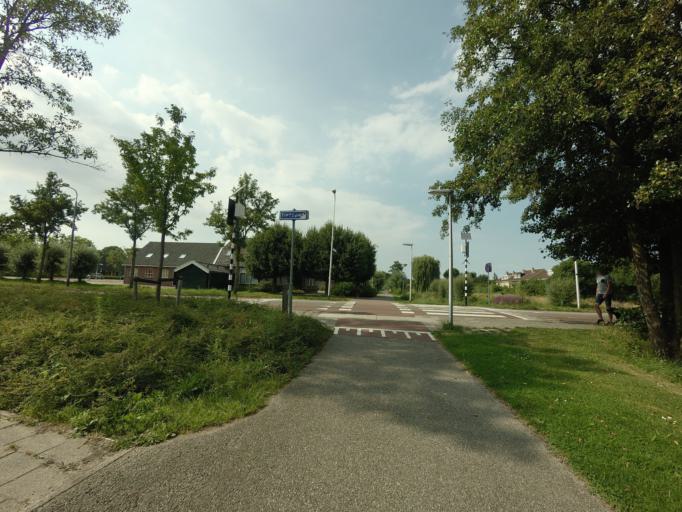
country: NL
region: South Holland
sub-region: Gemeente Nieuwkoop
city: Nieuwkoop
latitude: 52.1475
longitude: 4.7690
